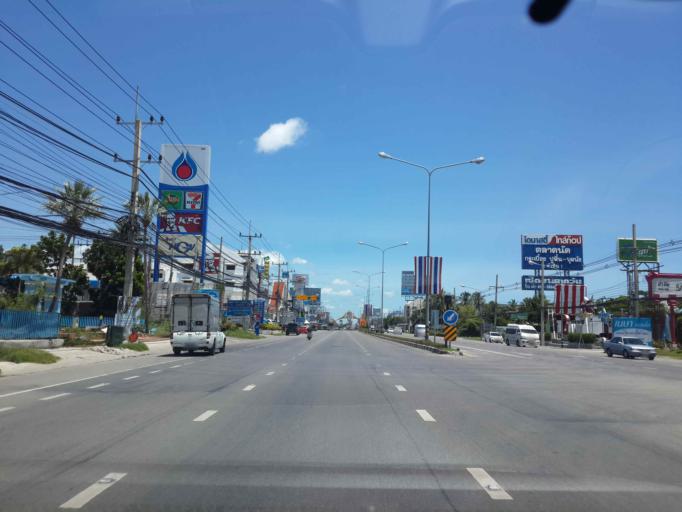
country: TH
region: Prachuap Khiri Khan
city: Hua Hin
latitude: 12.6156
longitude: 99.9503
